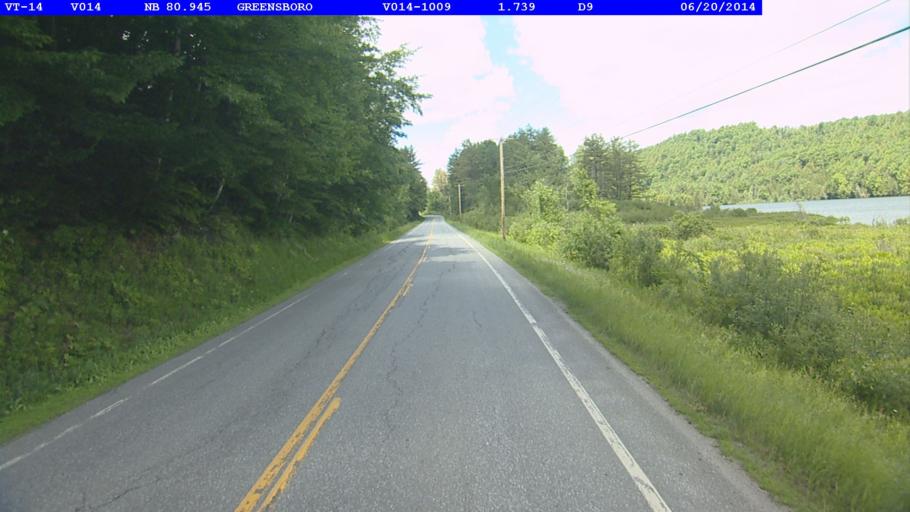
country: US
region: Vermont
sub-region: Caledonia County
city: Hardwick
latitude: 44.6038
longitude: -72.3582
